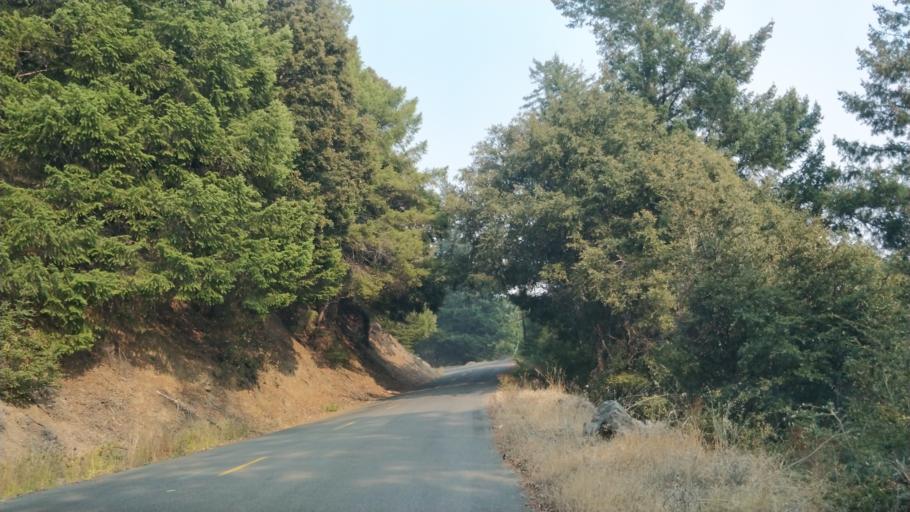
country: US
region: California
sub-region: Humboldt County
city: Rio Dell
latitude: 40.2682
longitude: -124.0858
